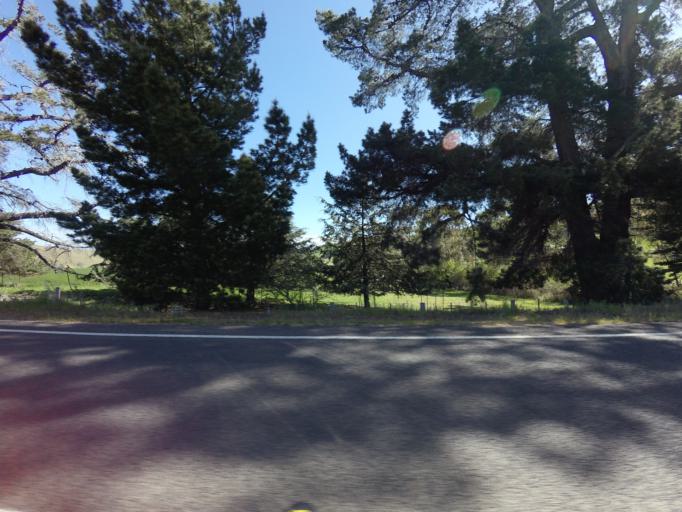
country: AU
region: Tasmania
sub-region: Derwent Valley
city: New Norfolk
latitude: -42.5648
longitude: 146.8799
